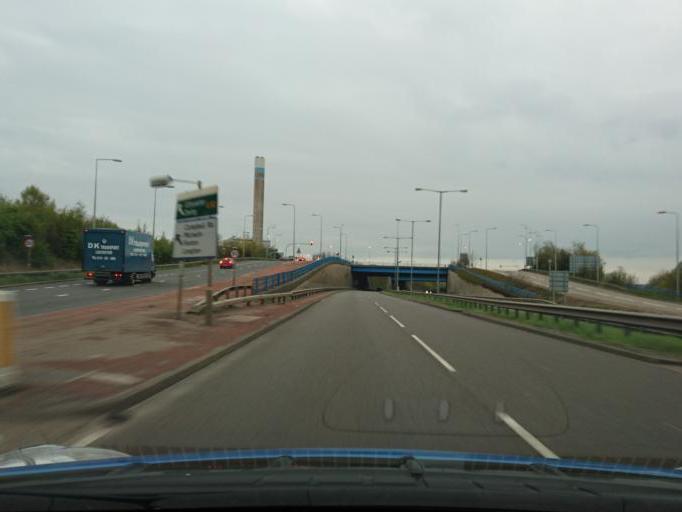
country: GB
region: England
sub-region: Stoke-on-Trent
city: Stoke-on-Trent
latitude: 52.9927
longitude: -2.1823
